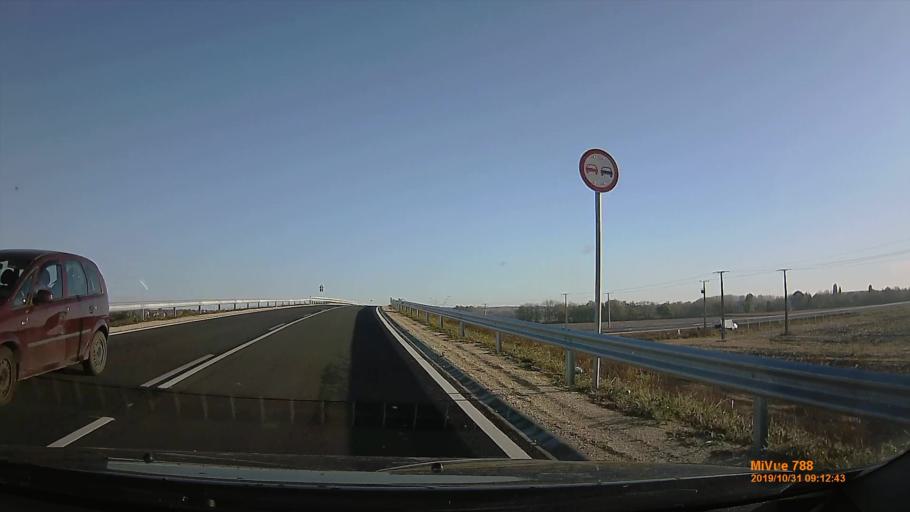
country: HU
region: Pest
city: Peteri
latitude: 47.3768
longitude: 19.3976
